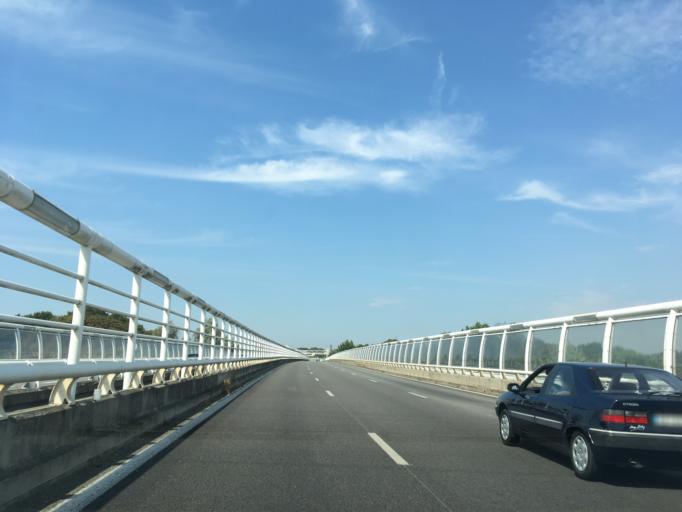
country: FR
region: Ile-de-France
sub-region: Departement des Yvelines
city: Carrieres-sur-Seine
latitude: 48.9052
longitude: 2.1955
